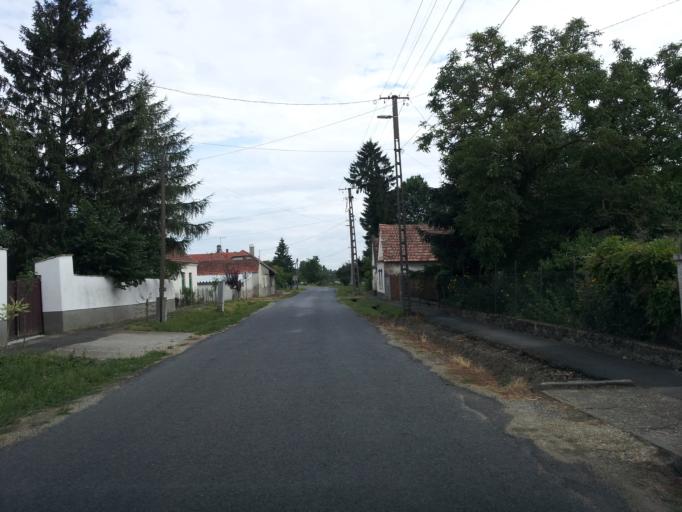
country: HU
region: Vas
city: Janoshaza
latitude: 47.1407
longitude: 17.1039
